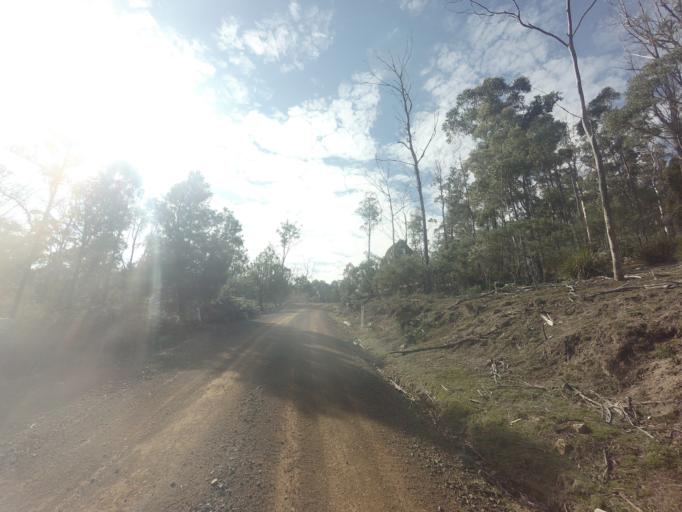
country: AU
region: Tasmania
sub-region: Sorell
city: Sorell
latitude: -42.5304
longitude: 147.4532
